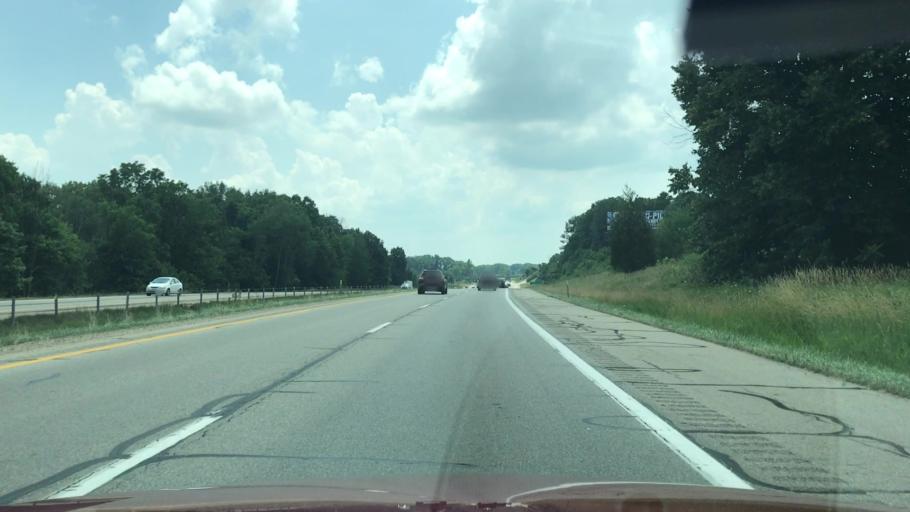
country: US
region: Michigan
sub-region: Allegan County
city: Wayland
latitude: 42.6041
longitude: -85.6603
